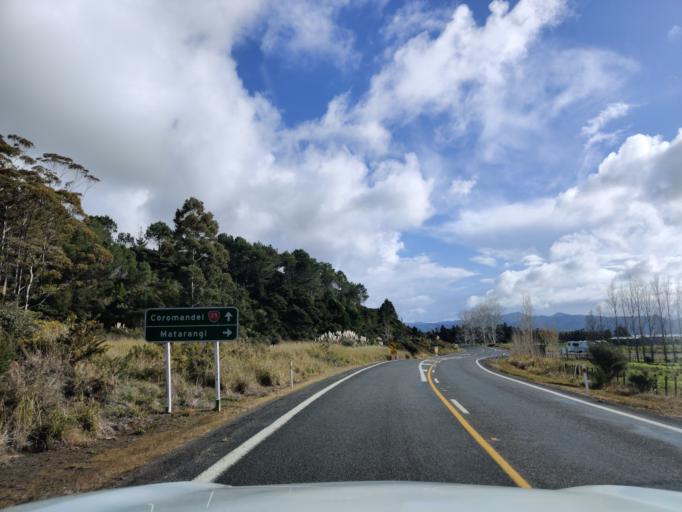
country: NZ
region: Waikato
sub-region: Thames-Coromandel District
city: Whitianga
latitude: -36.7486
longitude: 175.6723
